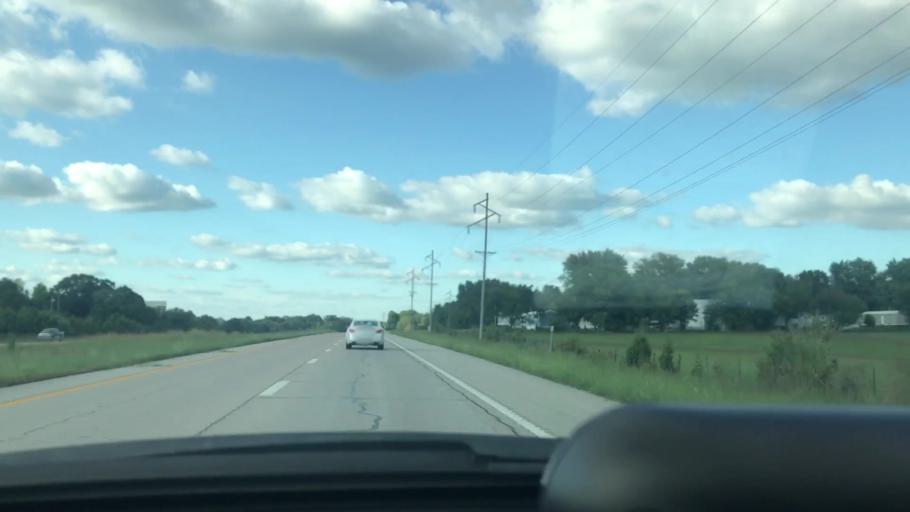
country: US
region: Missouri
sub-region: Pettis County
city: Sedalia
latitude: 38.6276
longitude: -93.2672
